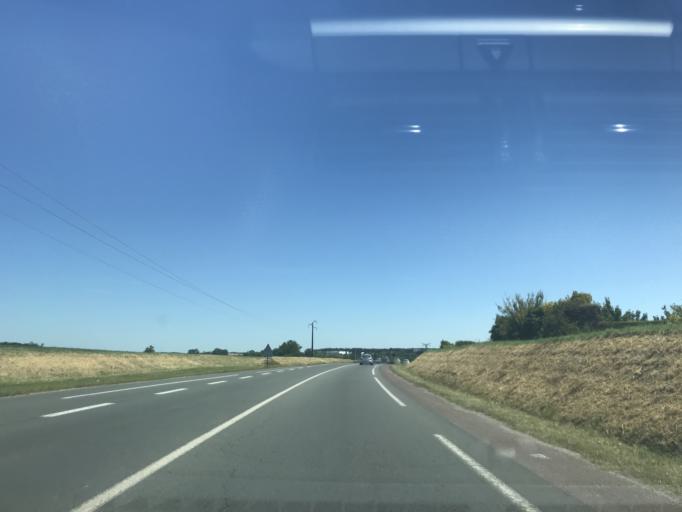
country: FR
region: Poitou-Charentes
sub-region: Departement de la Charente-Maritime
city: Royan
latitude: 45.6386
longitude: -1.0219
